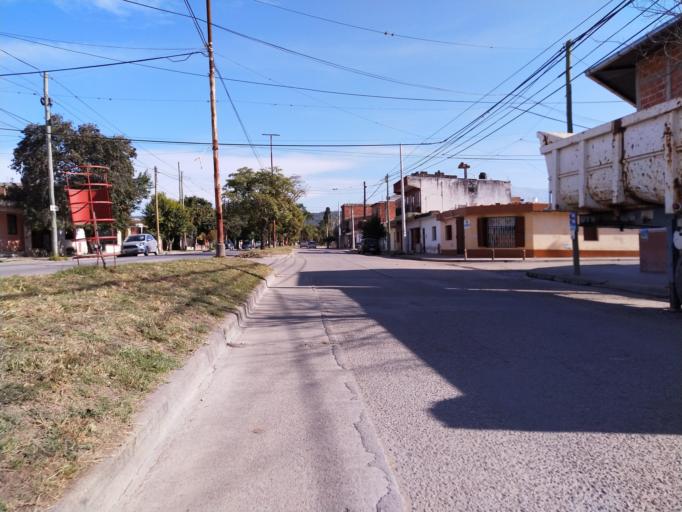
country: AR
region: Jujuy
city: San Salvador de Jujuy
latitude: -24.1991
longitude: -65.2806
